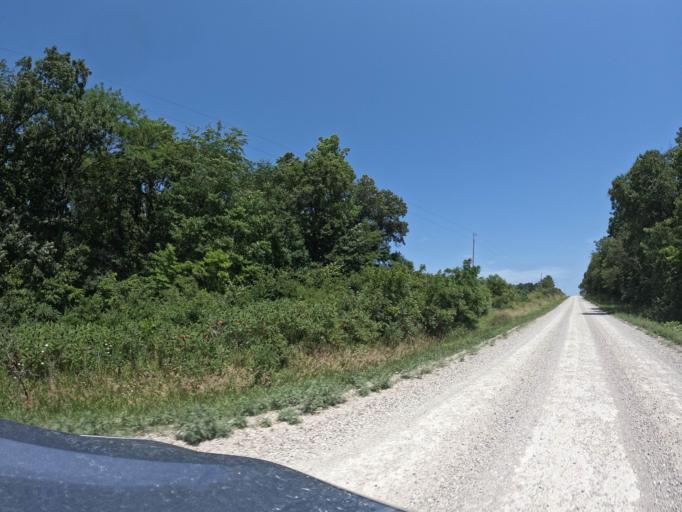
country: US
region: Iowa
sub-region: Henry County
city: Mount Pleasant
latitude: 40.9450
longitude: -91.6697
